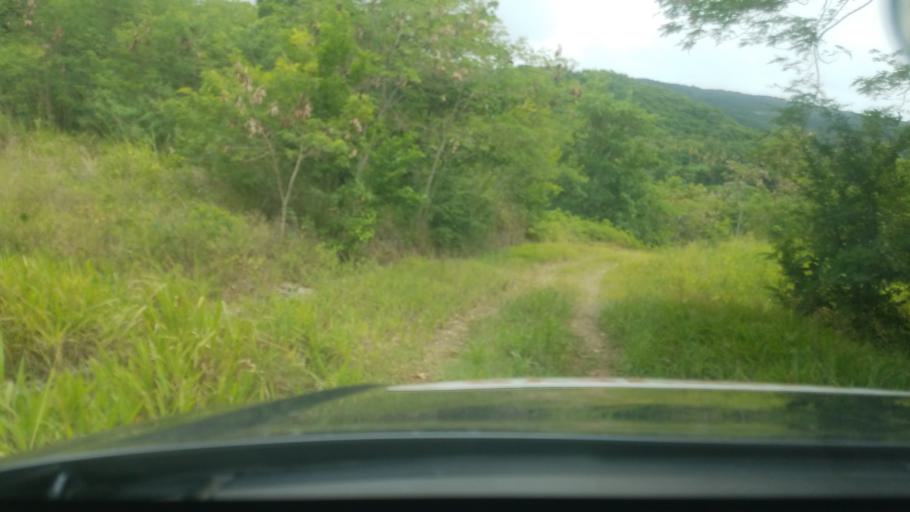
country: LC
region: Praslin
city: Praslin
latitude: 13.8647
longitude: -60.9019
